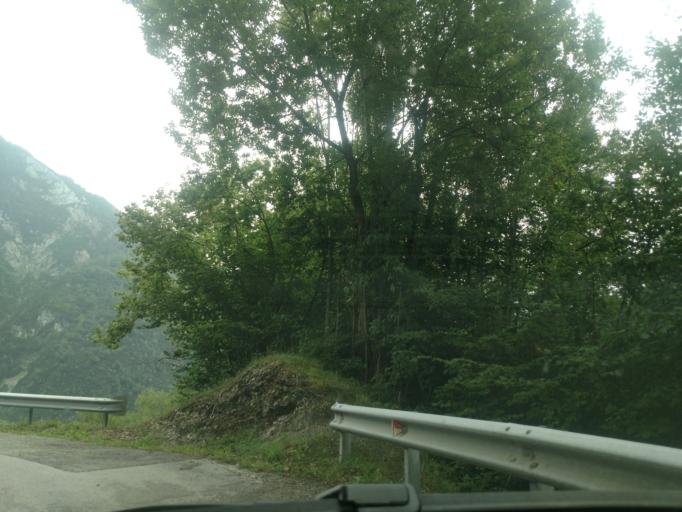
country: IT
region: Veneto
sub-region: Provincia di Belluno
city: Rivamonte Agordino
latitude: 46.2253
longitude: 11.9968
